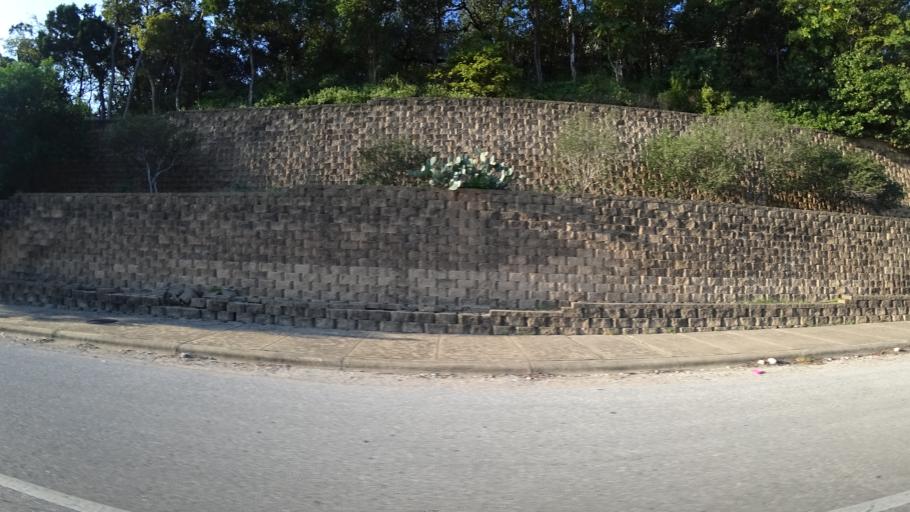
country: US
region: Texas
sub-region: Travis County
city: Rollingwood
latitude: 30.2670
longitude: -97.7852
